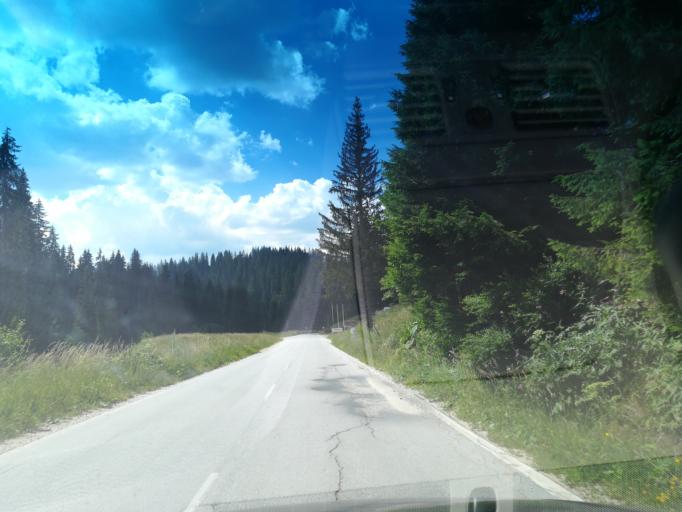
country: BG
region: Smolyan
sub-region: Obshtina Smolyan
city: Smolyan
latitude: 41.6558
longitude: 24.6869
